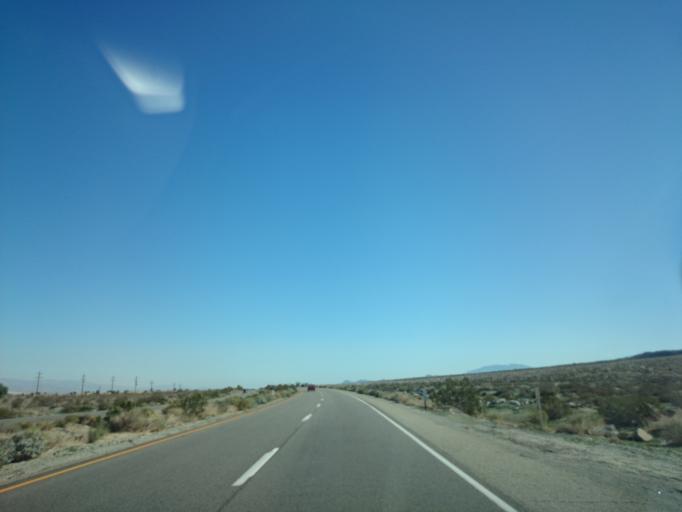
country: US
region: California
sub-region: Riverside County
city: Garnet
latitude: 33.8693
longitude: -116.5765
